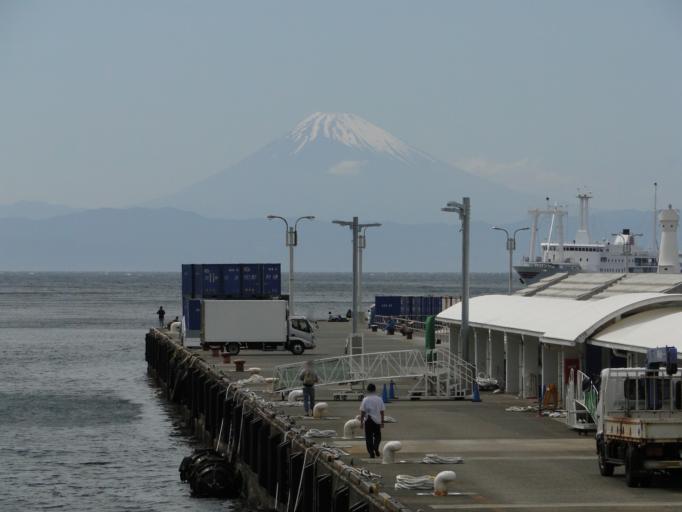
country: JP
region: Shizuoka
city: Ito
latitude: 34.7898
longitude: 139.3918
